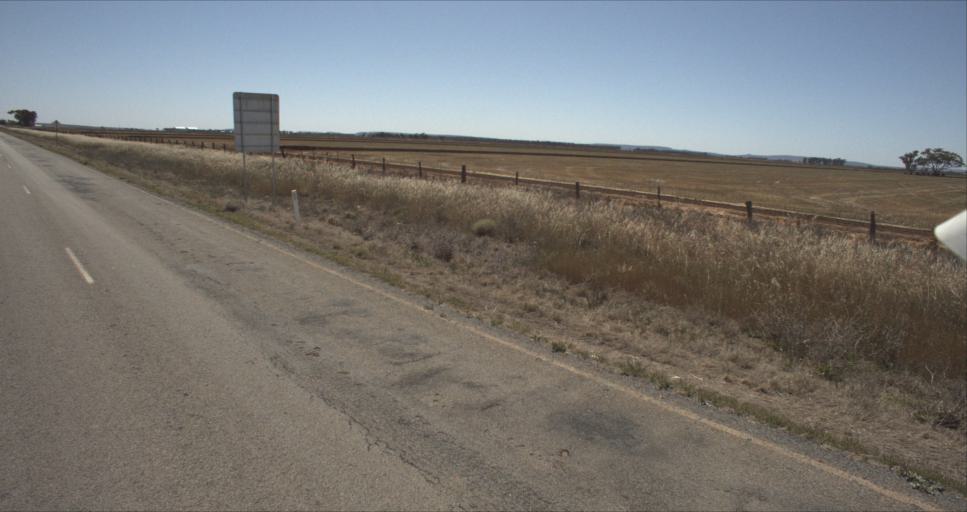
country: AU
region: New South Wales
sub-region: Leeton
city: Leeton
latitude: -34.5174
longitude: 146.2839
